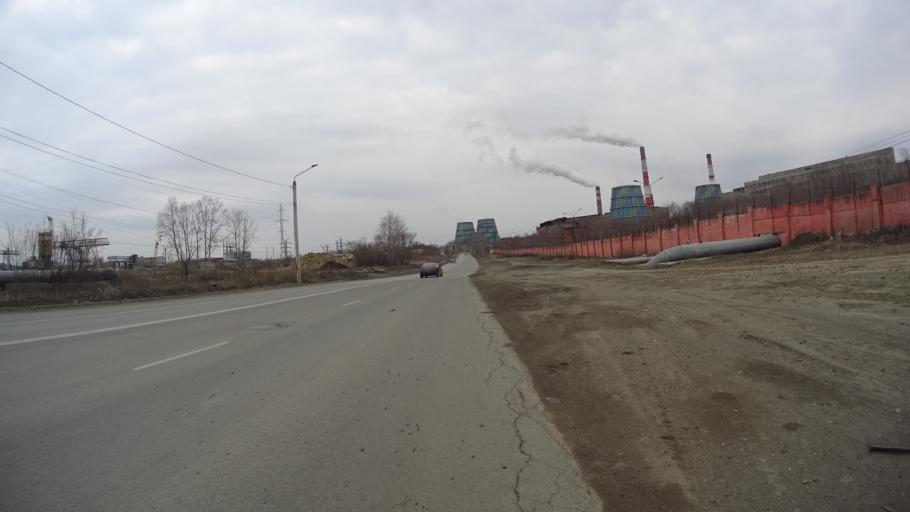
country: RU
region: Chelyabinsk
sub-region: Gorod Chelyabinsk
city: Chelyabinsk
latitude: 55.1577
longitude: 61.4885
